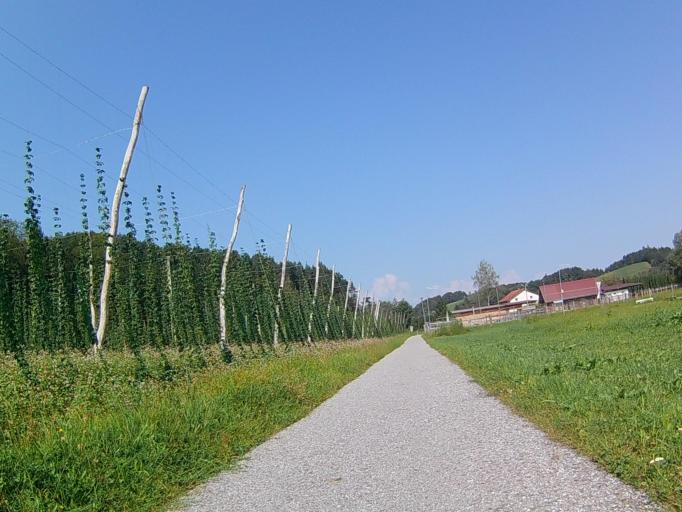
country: AT
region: Styria
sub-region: Politischer Bezirk Leibnitz
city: Leutschach
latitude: 46.6645
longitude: 15.4572
